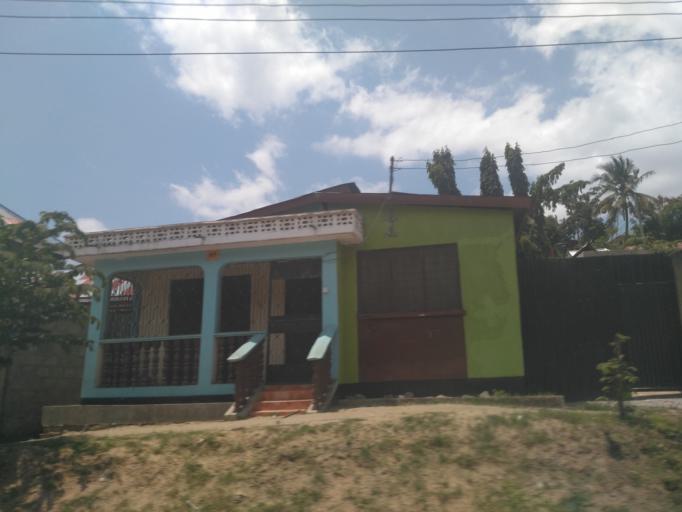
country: TZ
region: Dar es Salaam
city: Dar es Salaam
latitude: -6.8862
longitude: 39.2749
